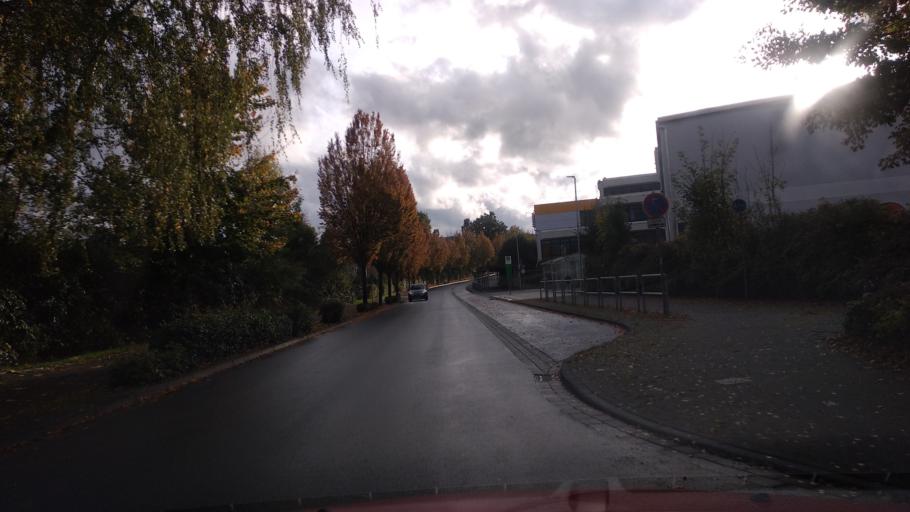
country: DE
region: North Rhine-Westphalia
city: Beverungen
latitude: 51.6674
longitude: 9.3695
